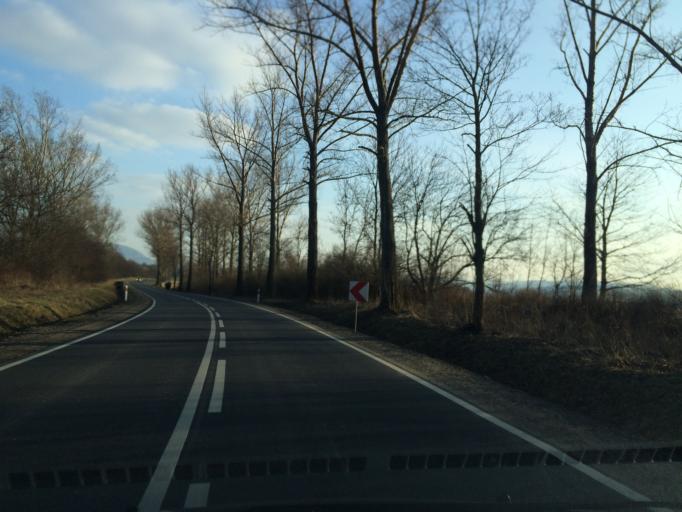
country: PL
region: Lower Silesian Voivodeship
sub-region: Powiat klodzki
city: Miedzylesie
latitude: 50.2266
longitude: 16.6771
